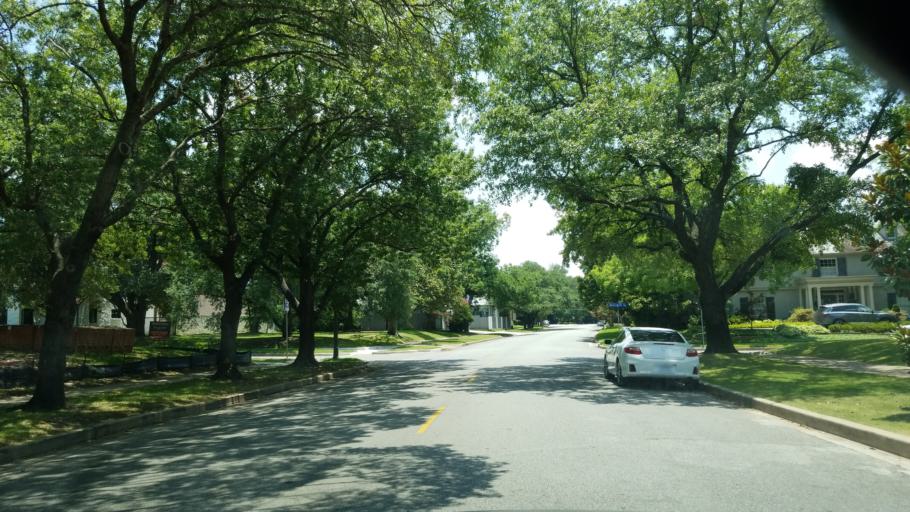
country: US
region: Texas
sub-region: Dallas County
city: Highland Park
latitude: 32.8305
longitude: -96.8098
